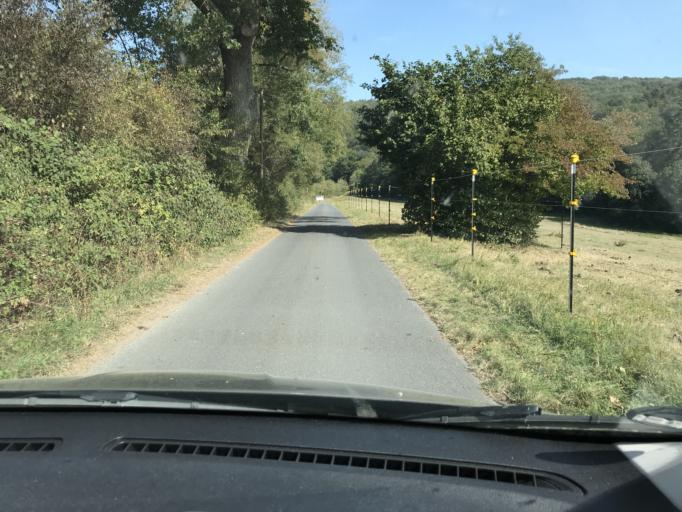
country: DE
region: Hesse
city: Hochst im Odenwald
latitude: 49.8370
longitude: 8.9905
